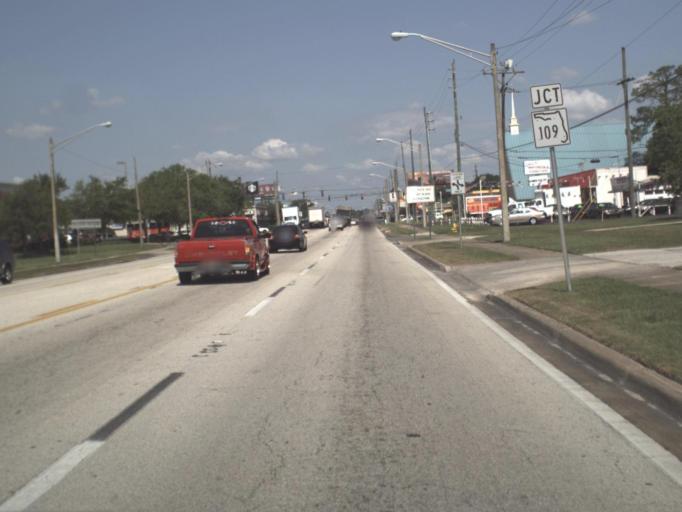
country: US
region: Florida
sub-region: Duval County
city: Jacksonville
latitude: 30.2920
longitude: -81.5999
